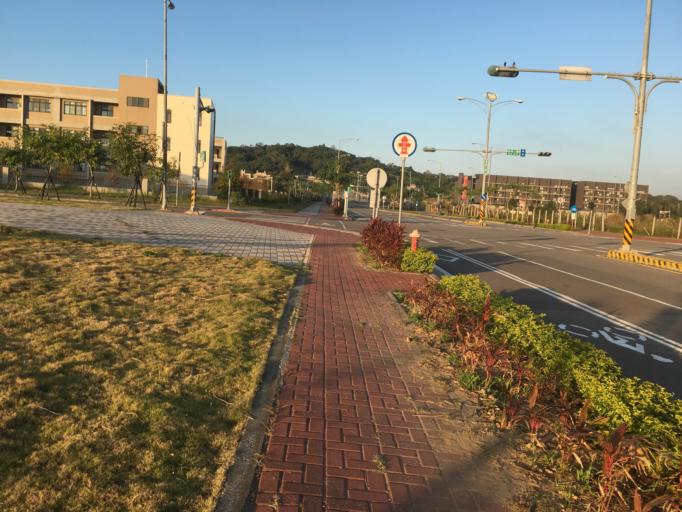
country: TW
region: Taiwan
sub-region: Miaoli
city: Miaoli
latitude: 24.6095
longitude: 120.8274
